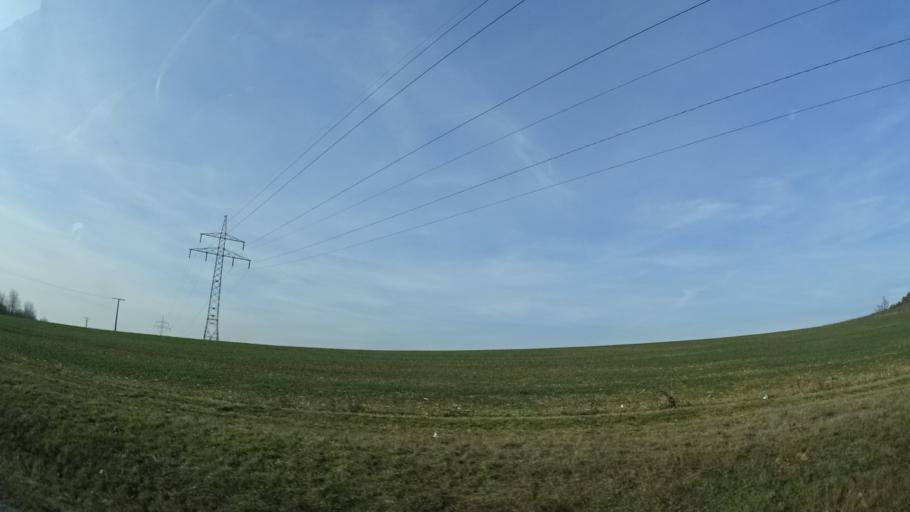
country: DE
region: Bavaria
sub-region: Regierungsbezirk Unterfranken
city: Heustreu
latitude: 50.3370
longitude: 10.2327
